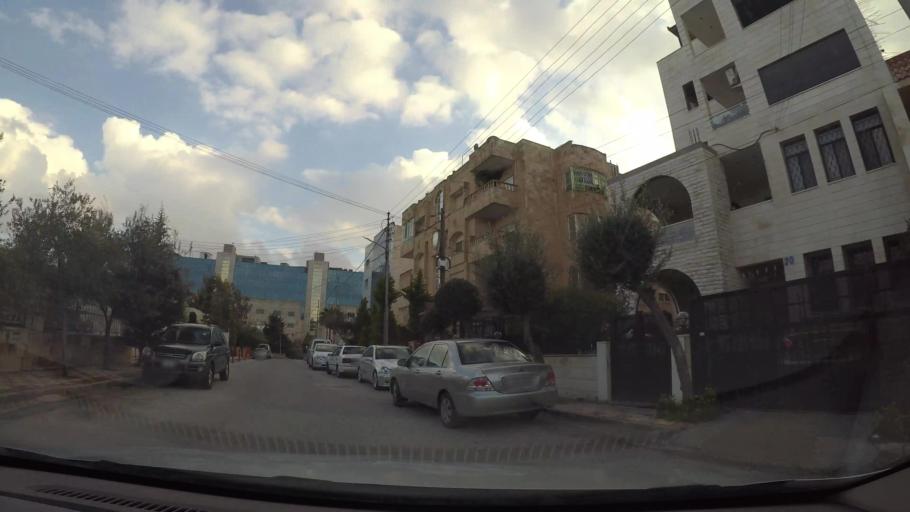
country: JO
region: Amman
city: Wadi as Sir
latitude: 31.9780
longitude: 35.8555
